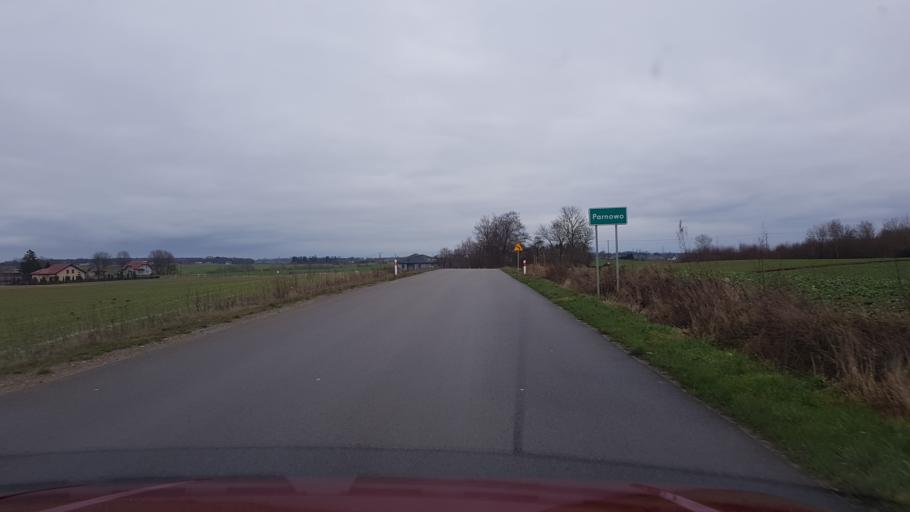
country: PL
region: West Pomeranian Voivodeship
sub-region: Powiat koszalinski
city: Mielno
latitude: 54.1700
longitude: 16.0100
